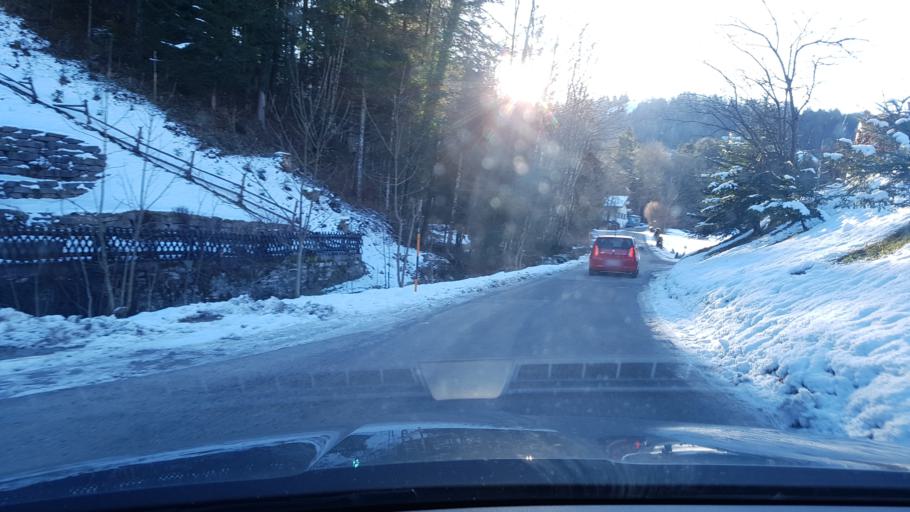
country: AT
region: Salzburg
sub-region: Politischer Bezirk Hallein
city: Scheffau am Tennengebirge
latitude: 47.6497
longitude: 13.2169
